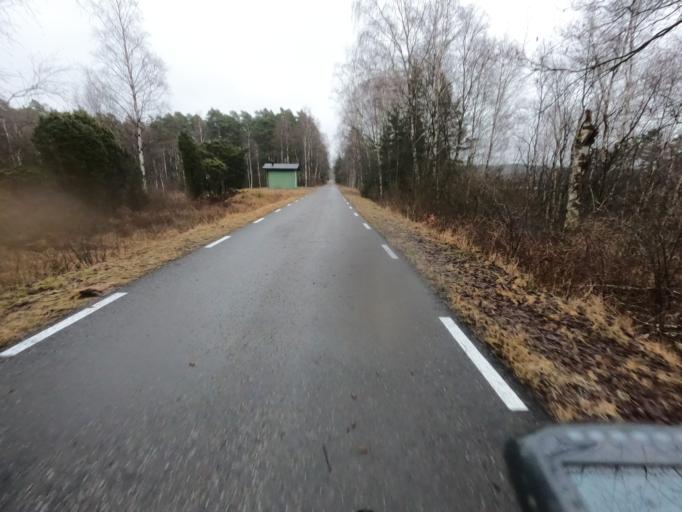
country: SE
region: Halland
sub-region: Halmstads Kommun
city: Aled
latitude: 56.7078
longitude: 13.0492
